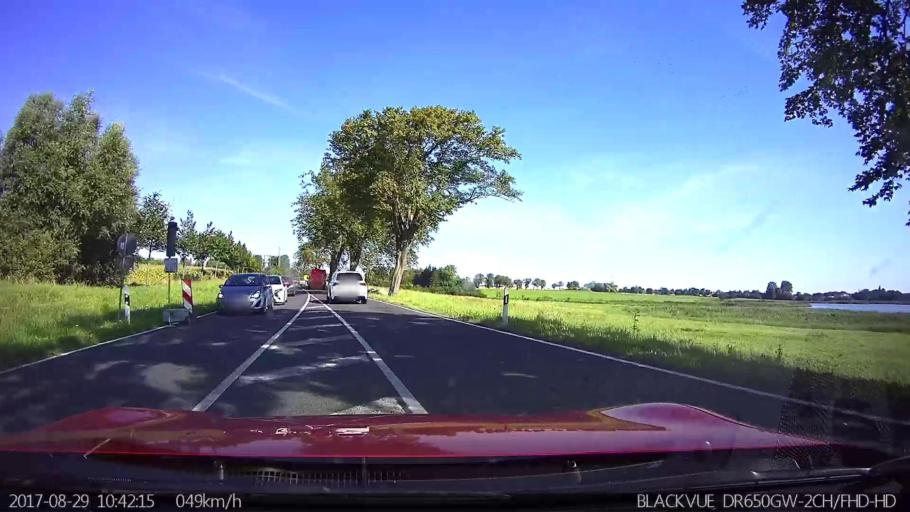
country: DE
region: Mecklenburg-Vorpommern
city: Franzburg
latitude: 54.1903
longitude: 12.8667
